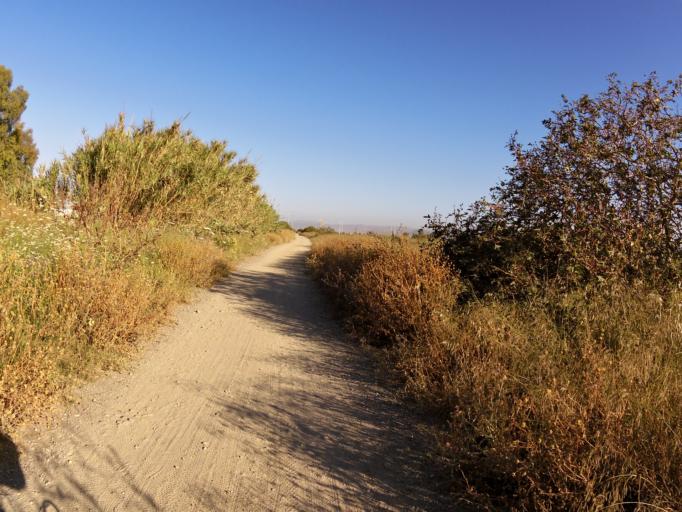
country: ES
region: Andalusia
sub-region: Provincia de Malaga
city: Torremolinos
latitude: 36.6758
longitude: -4.4715
